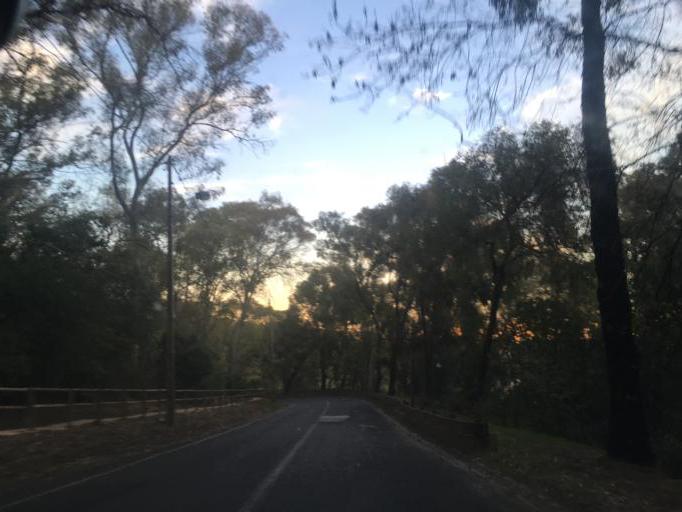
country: PT
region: Setubal
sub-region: Almada
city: Pragal
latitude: 38.7212
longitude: -9.1826
